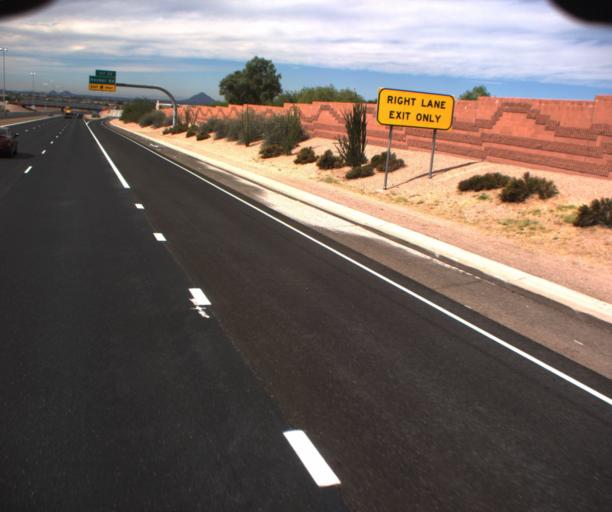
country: US
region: Arizona
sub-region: Maricopa County
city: Fountain Hills
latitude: 33.4756
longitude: -111.6940
